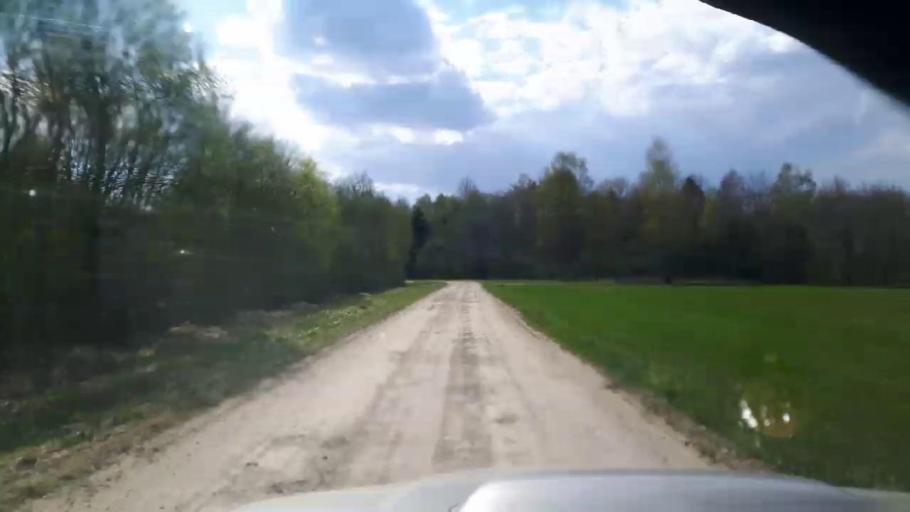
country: EE
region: Paernumaa
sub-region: Sindi linn
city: Sindi
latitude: 58.4297
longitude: 24.7698
